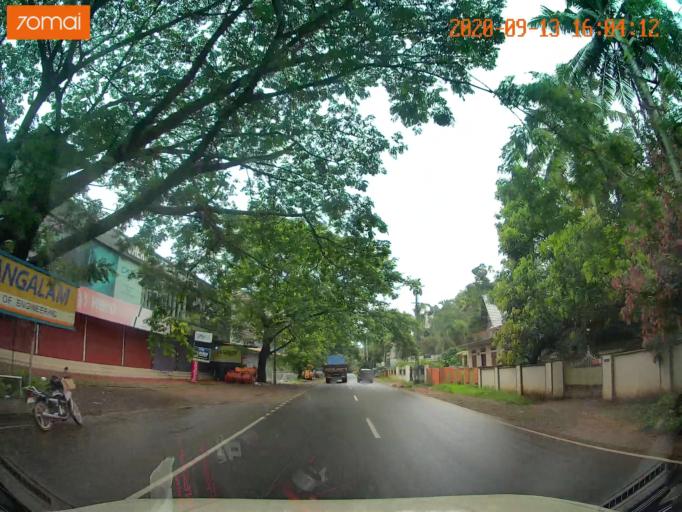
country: IN
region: Kerala
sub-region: Kottayam
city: Palackattumala
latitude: 9.6724
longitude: 76.5687
